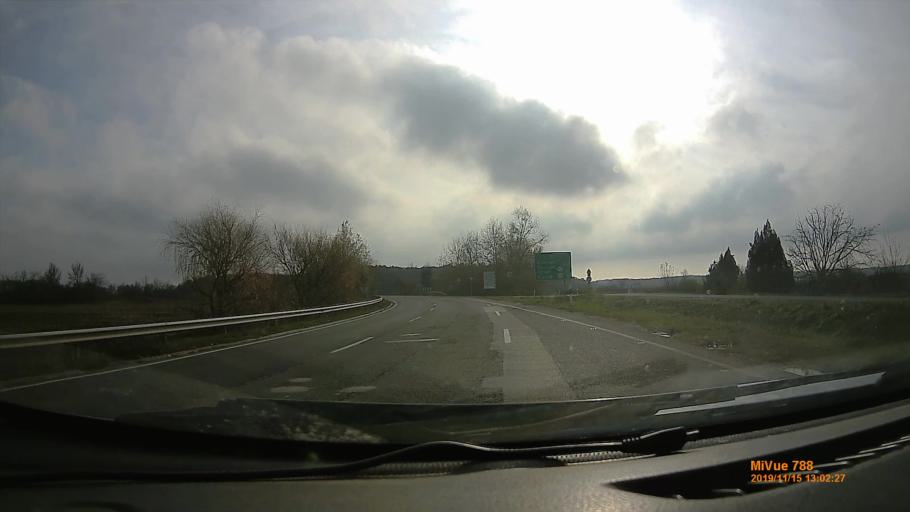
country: HU
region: Bekes
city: Gyula
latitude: 46.6521
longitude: 21.2379
